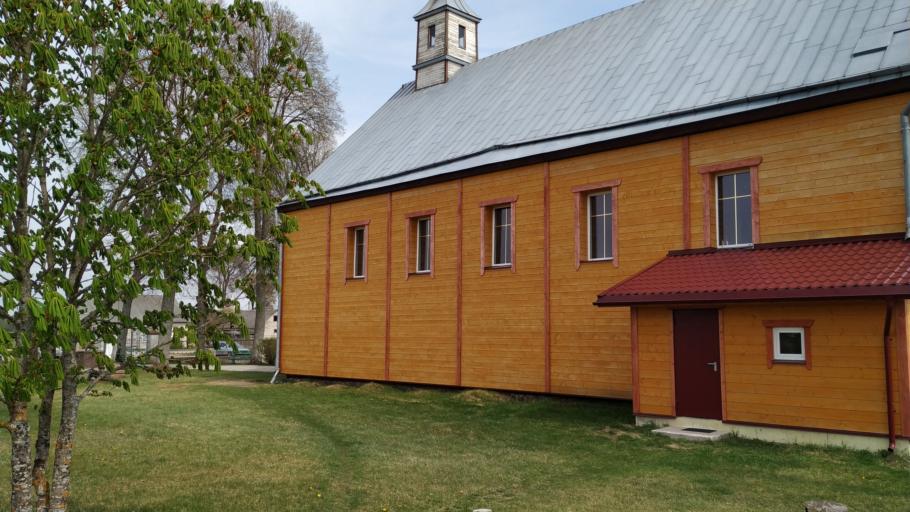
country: LT
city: Baltoji Voke
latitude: 54.4320
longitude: 25.1502
